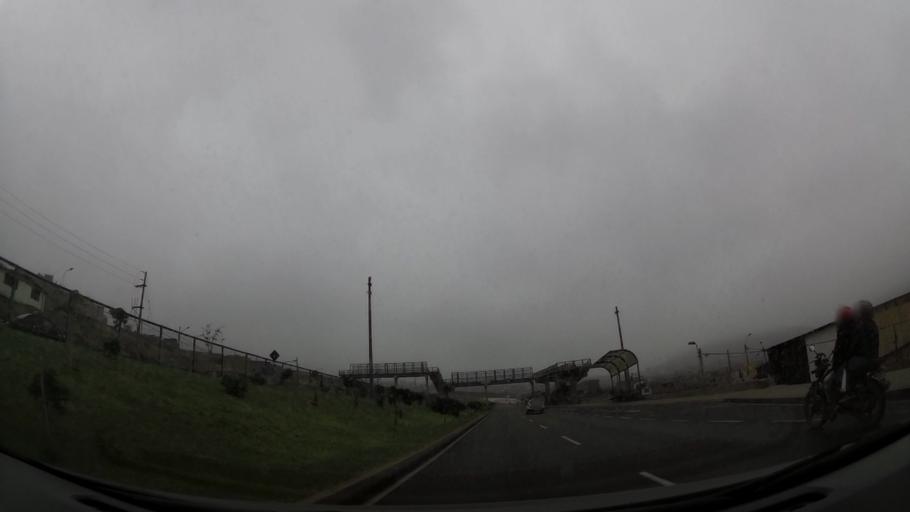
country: PE
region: Lima
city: Ventanilla
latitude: -11.8561
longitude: -77.1300
